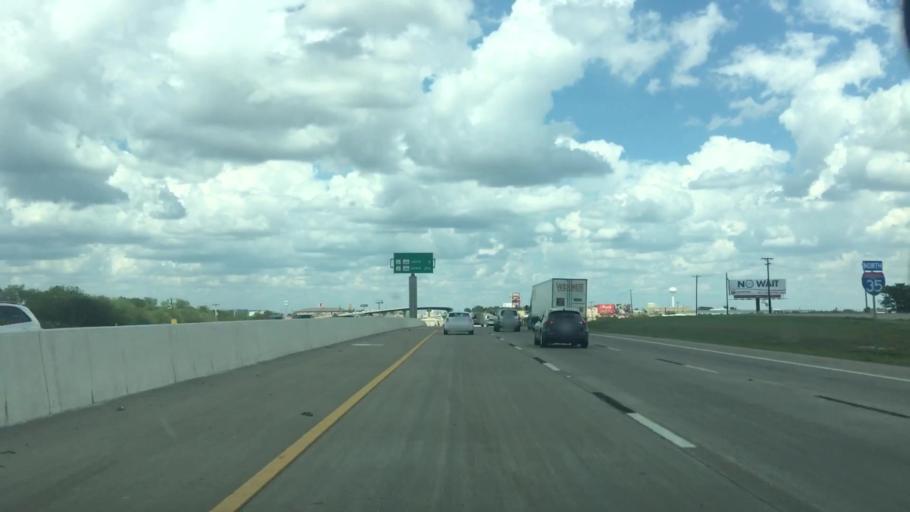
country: US
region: Texas
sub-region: McLennan County
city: Hewitt
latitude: 31.4493
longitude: -97.1771
